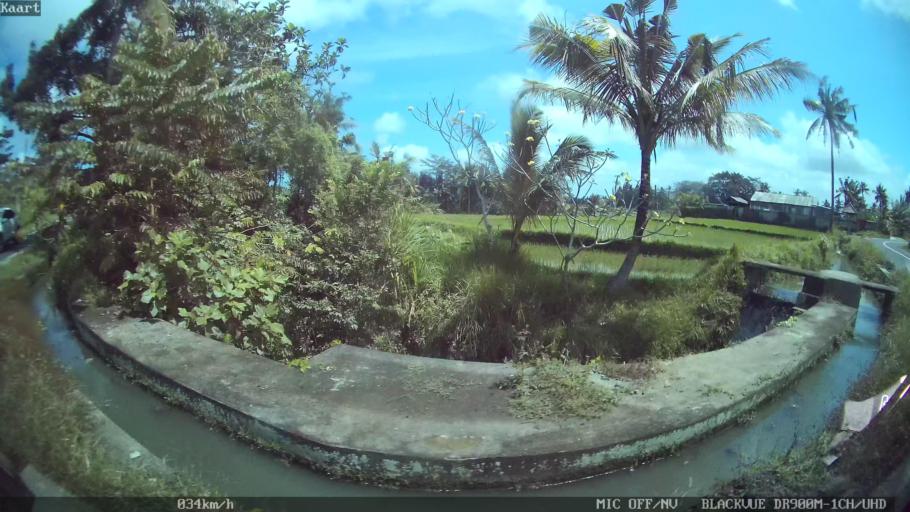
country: ID
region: Bali
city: Banjar Apuan Kaja
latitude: -8.4889
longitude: 115.3430
